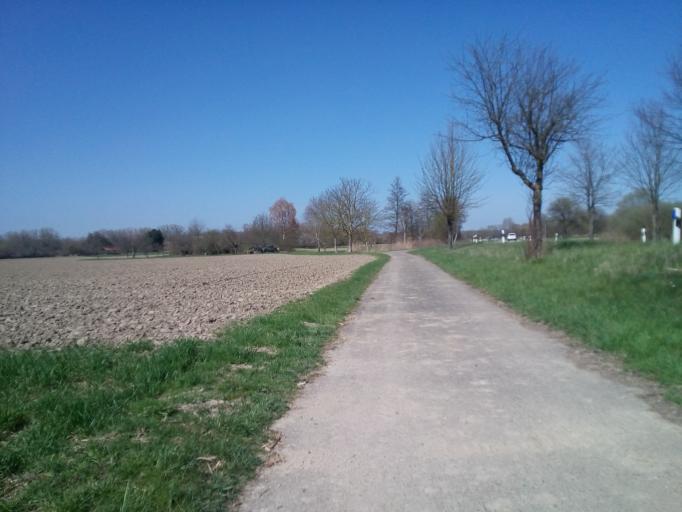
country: FR
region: Alsace
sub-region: Departement du Bas-Rhin
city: La Wantzenau
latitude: 48.6322
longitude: 7.8611
